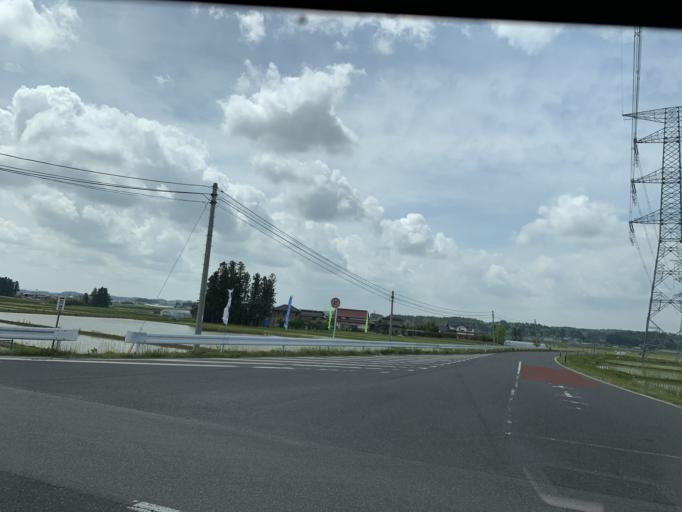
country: JP
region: Iwate
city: Ichinoseki
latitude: 38.8031
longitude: 141.0106
